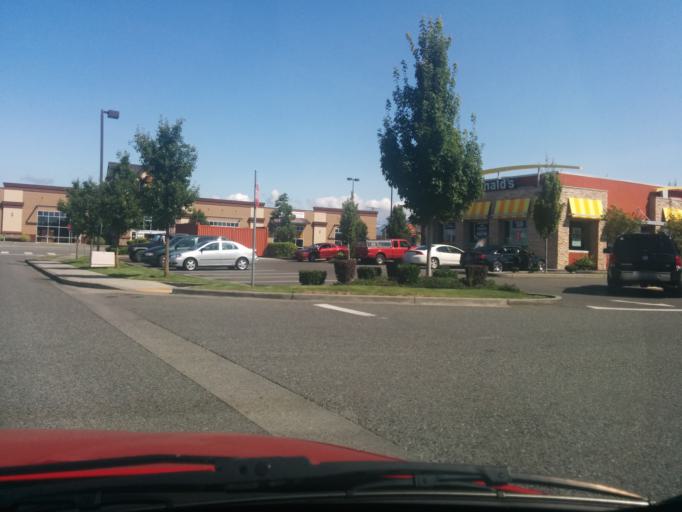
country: US
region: Washington
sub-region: Skagit County
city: Mount Vernon
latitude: 48.4481
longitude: -122.3367
